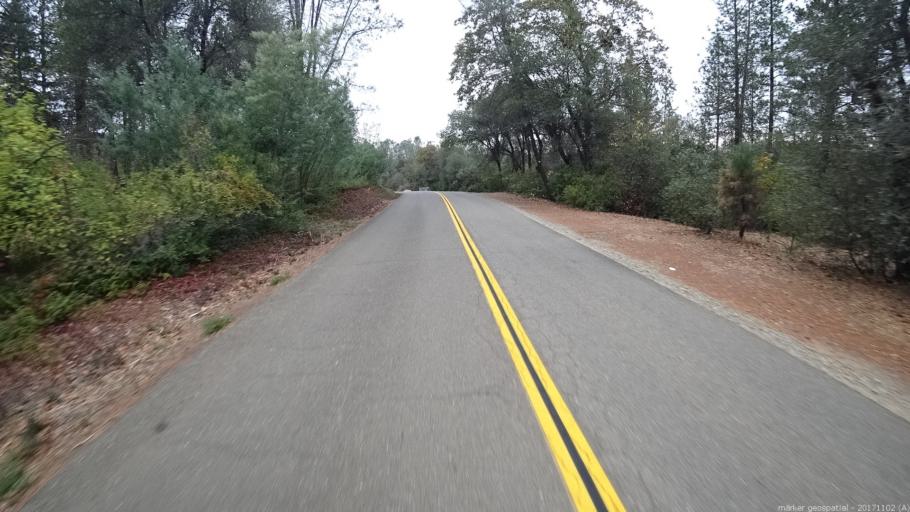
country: US
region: California
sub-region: Shasta County
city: Central Valley (historical)
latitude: 40.6636
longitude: -122.4021
